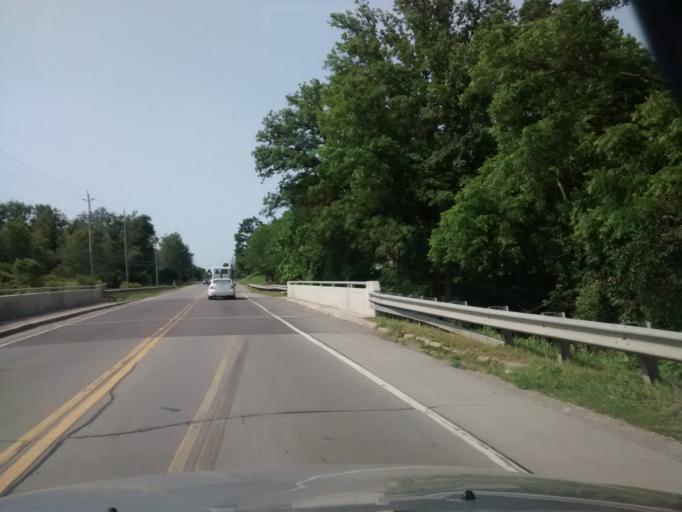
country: CA
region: Ontario
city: Hamilton
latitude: 43.1441
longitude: -79.7946
